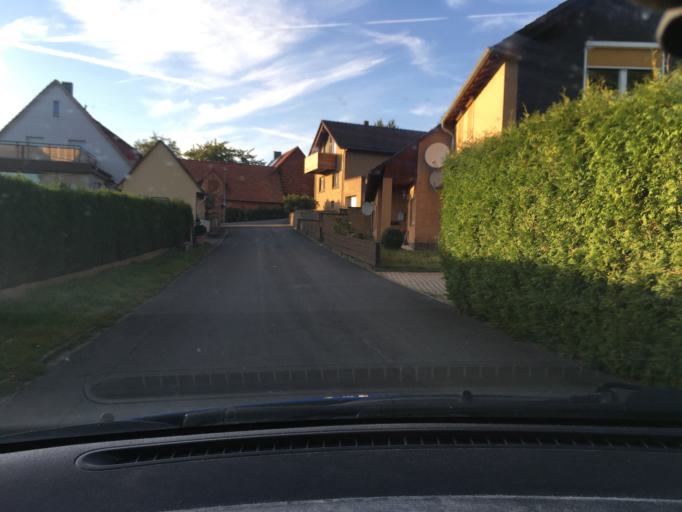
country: DE
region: Lower Saxony
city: Lauenau
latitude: 52.2864
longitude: 9.3978
